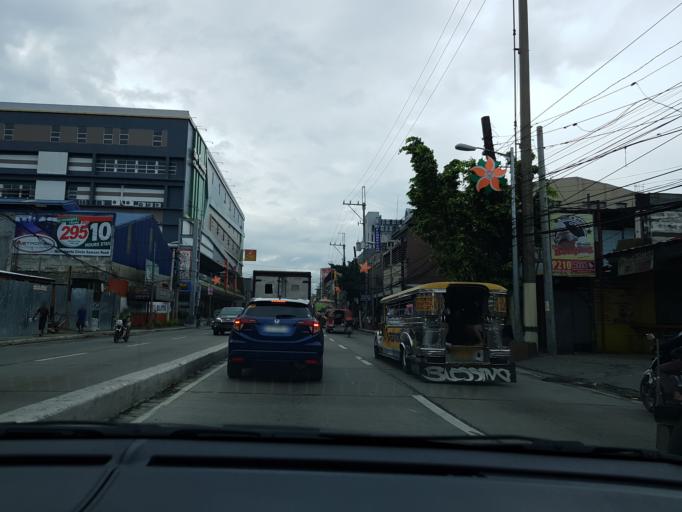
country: PH
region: Metro Manila
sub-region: Caloocan City
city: Niugan
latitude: 14.6607
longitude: 120.9841
